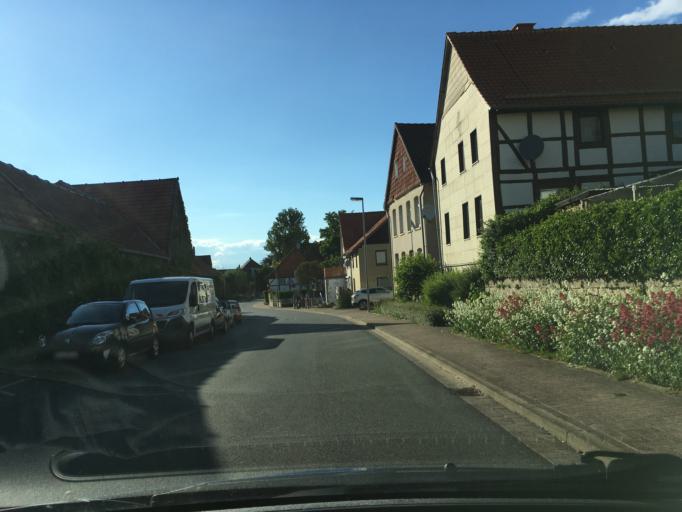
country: DE
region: Lower Saxony
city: Duingen
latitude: 52.0035
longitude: 9.7038
